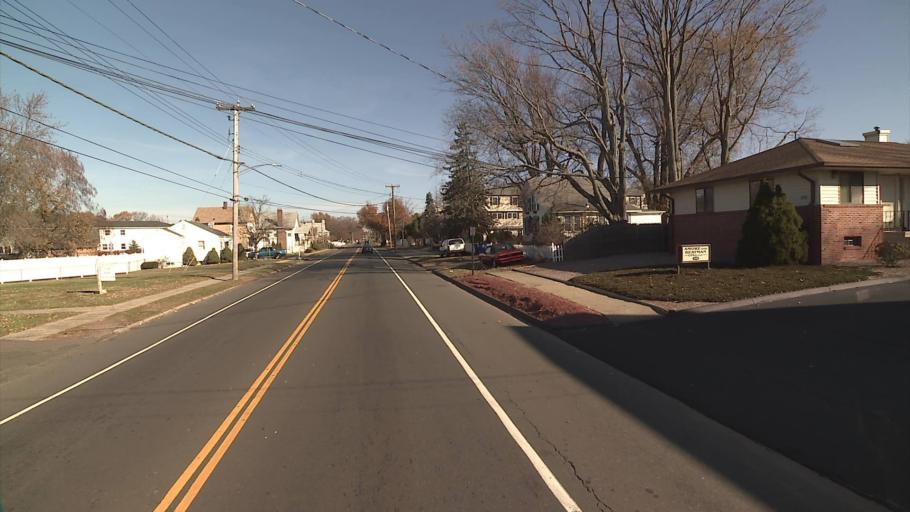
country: US
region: Connecticut
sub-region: New Haven County
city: East Haven
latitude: 41.3284
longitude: -72.8777
